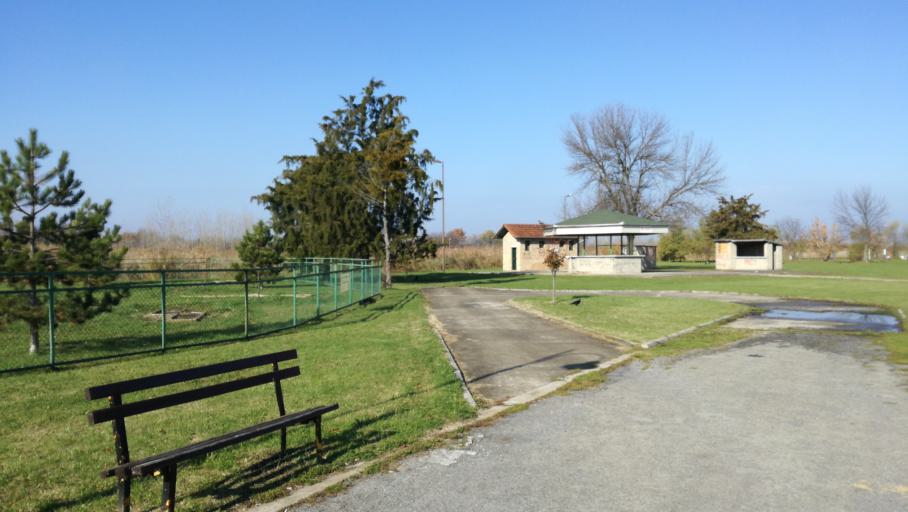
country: RS
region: Autonomna Pokrajina Vojvodina
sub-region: Severnobanatski Okrug
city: Kikinda
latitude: 45.8371
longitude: 20.4660
